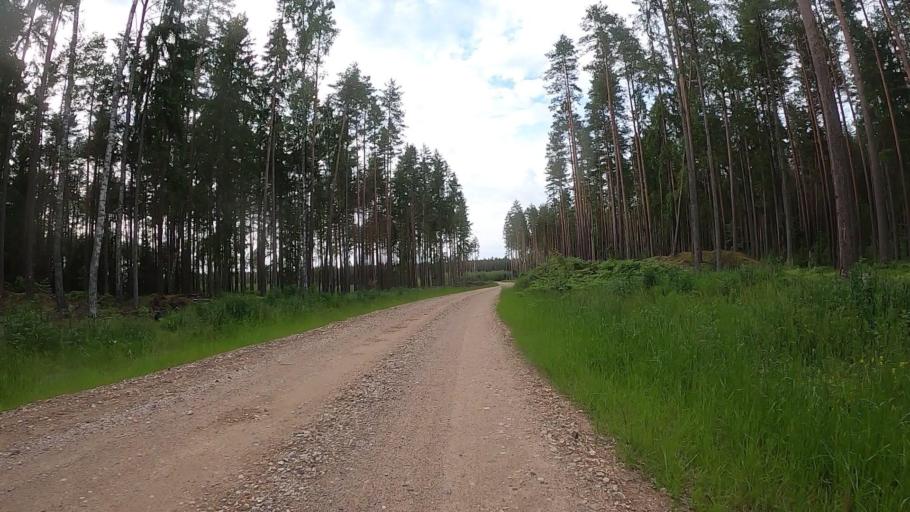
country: LV
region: Olaine
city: Olaine
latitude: 56.7666
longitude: 23.9033
